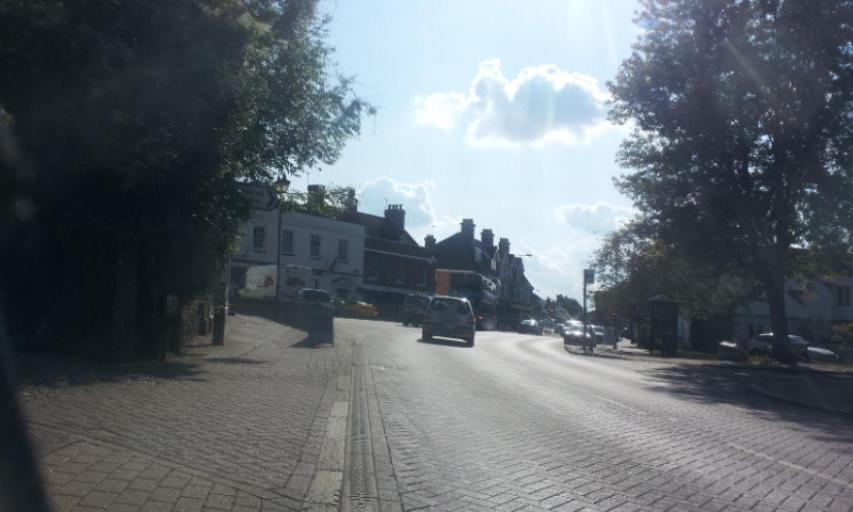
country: GB
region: England
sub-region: Kent
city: Hadlow
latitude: 51.2244
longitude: 0.3395
